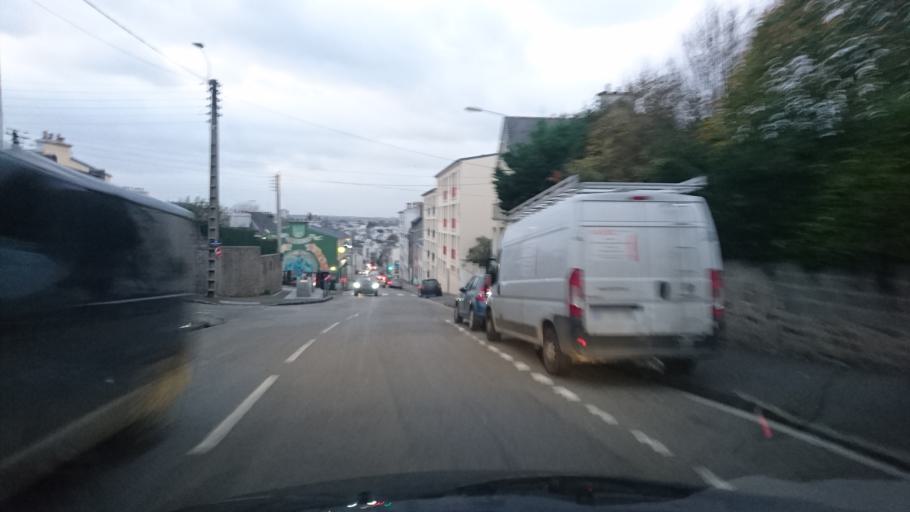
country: FR
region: Brittany
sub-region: Departement du Finistere
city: Brest
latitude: 48.3990
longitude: -4.4842
